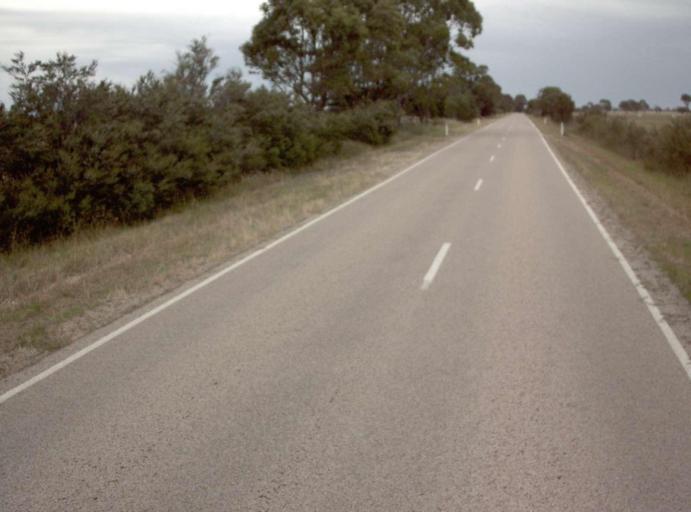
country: AU
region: Victoria
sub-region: East Gippsland
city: Bairnsdale
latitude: -37.8864
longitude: 147.5576
